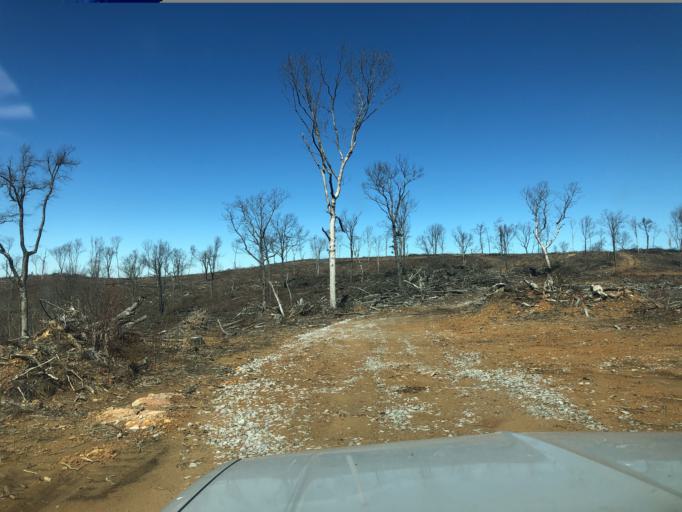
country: US
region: Tennessee
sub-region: Cumberland County
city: Fairfield Glade
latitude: 35.9717
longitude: -84.7659
